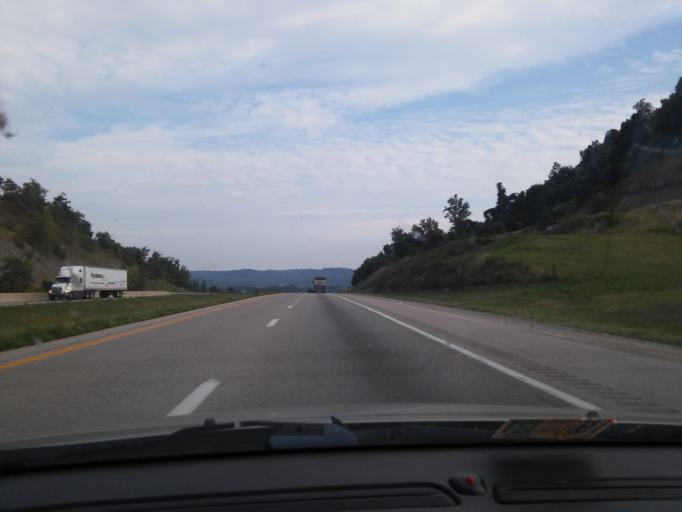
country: US
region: Ohio
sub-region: Pike County
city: Waverly
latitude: 39.2275
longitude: -82.8318
